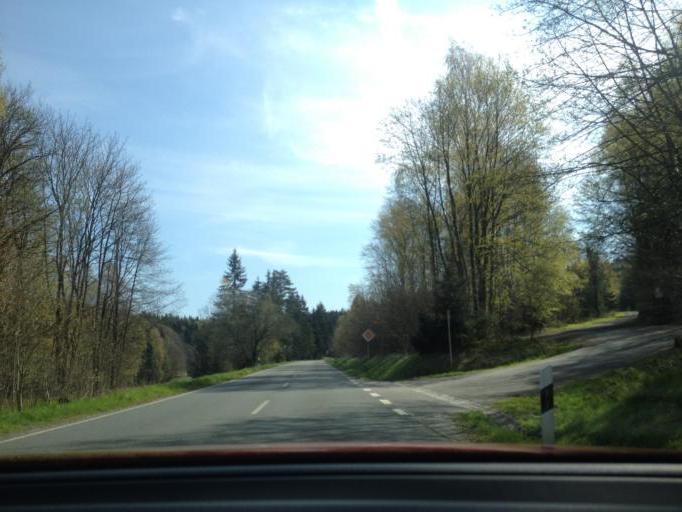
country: DE
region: Bavaria
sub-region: Upper Franconia
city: Gefrees
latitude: 50.0921
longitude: 11.7558
